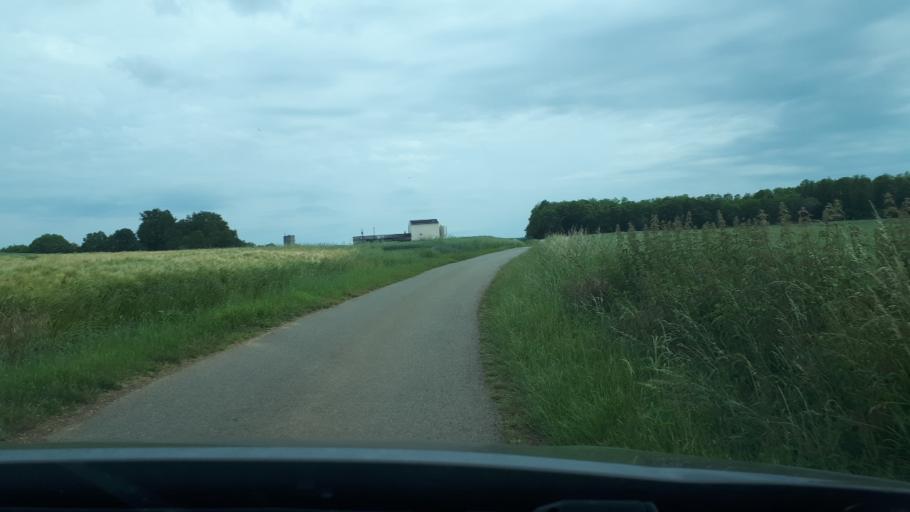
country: FR
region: Centre
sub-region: Departement du Cher
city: Sancerre
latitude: 47.3153
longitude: 2.7421
